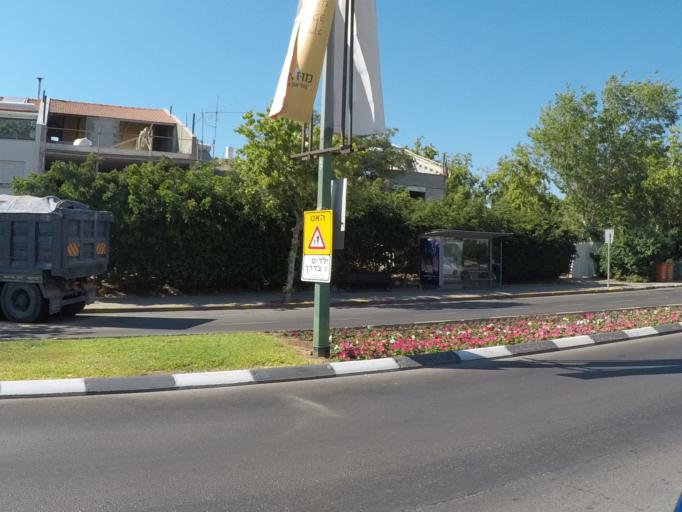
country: IL
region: Tel Aviv
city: Ramat Gan
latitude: 32.1040
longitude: 34.7976
